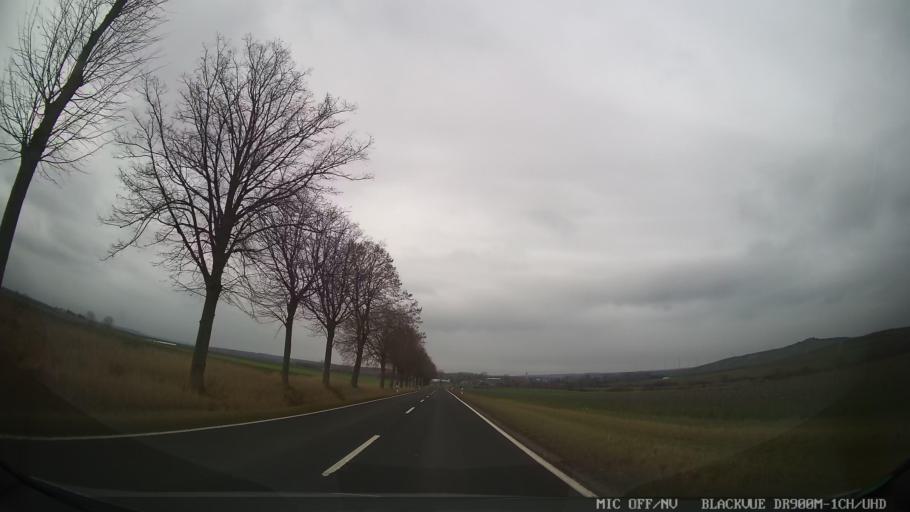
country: DE
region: Rheinland-Pfalz
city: Gau-Odernheim
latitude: 49.7755
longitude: 8.2200
